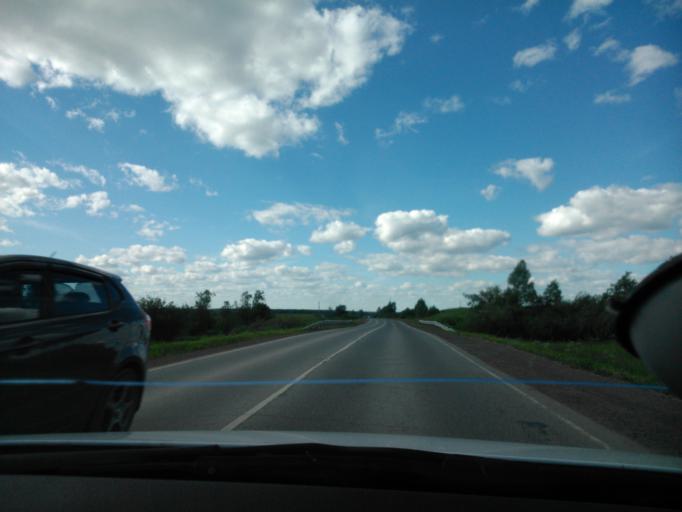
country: RU
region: Perm
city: Ust'-Kachka
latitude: 57.9307
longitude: 55.7611
